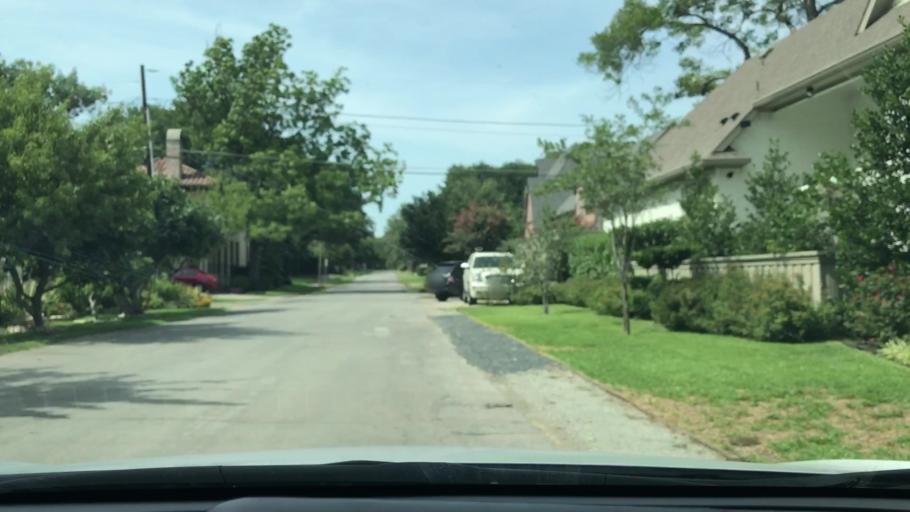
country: US
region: Texas
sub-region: Dallas County
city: University Park
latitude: 32.8824
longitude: -96.7900
